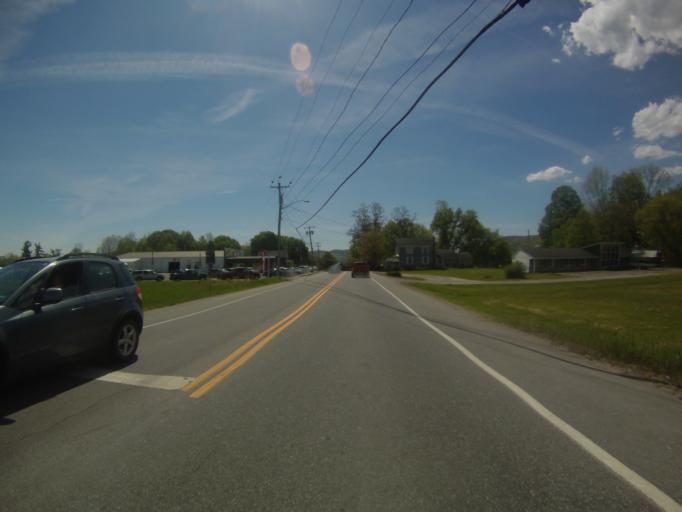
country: US
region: New York
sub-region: Essex County
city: Ticonderoga
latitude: 43.8546
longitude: -73.4381
